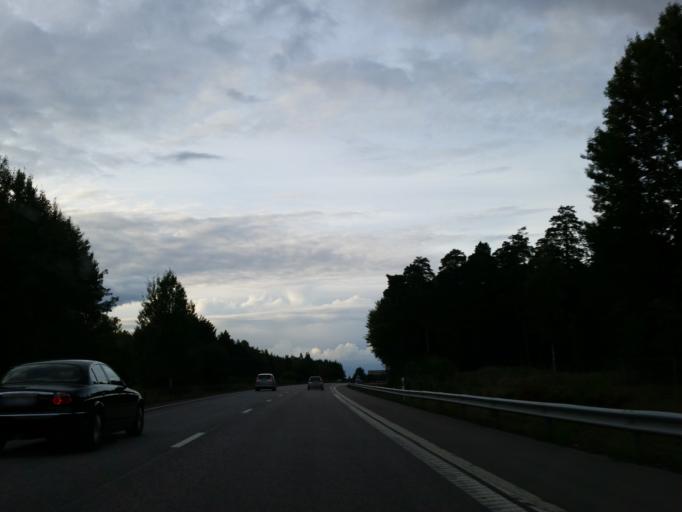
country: SE
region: Uppsala
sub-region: Uppsala Kommun
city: Alsike
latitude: 59.7890
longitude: 17.7762
